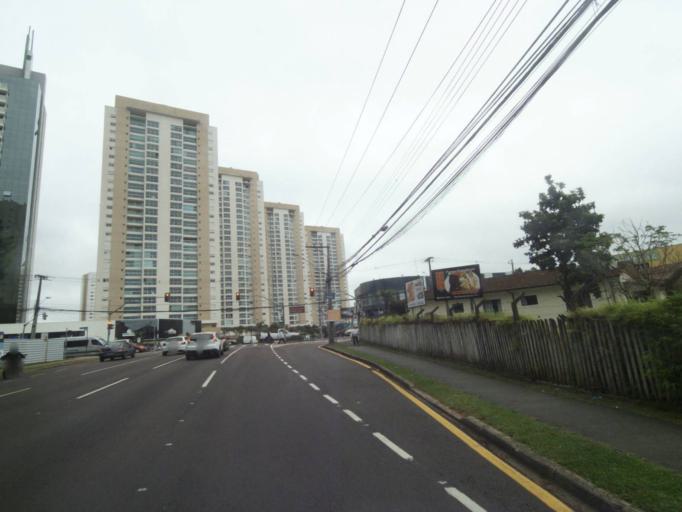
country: BR
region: Parana
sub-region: Curitiba
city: Curitiba
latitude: -25.4401
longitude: -49.3454
